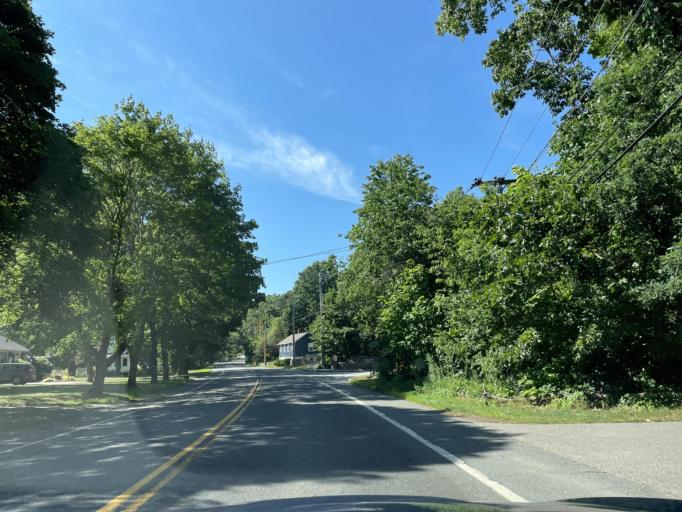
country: US
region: Massachusetts
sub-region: Worcester County
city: Northbridge
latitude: 42.1511
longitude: -71.6416
